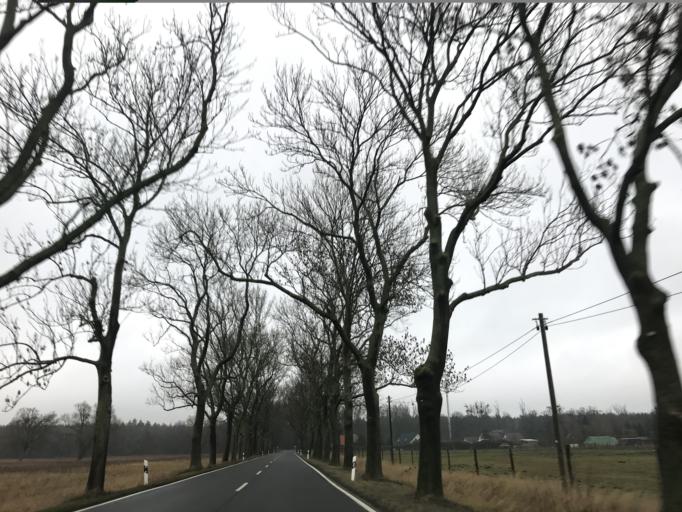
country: DE
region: Brandenburg
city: Brieselang
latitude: 52.6119
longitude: 12.9653
